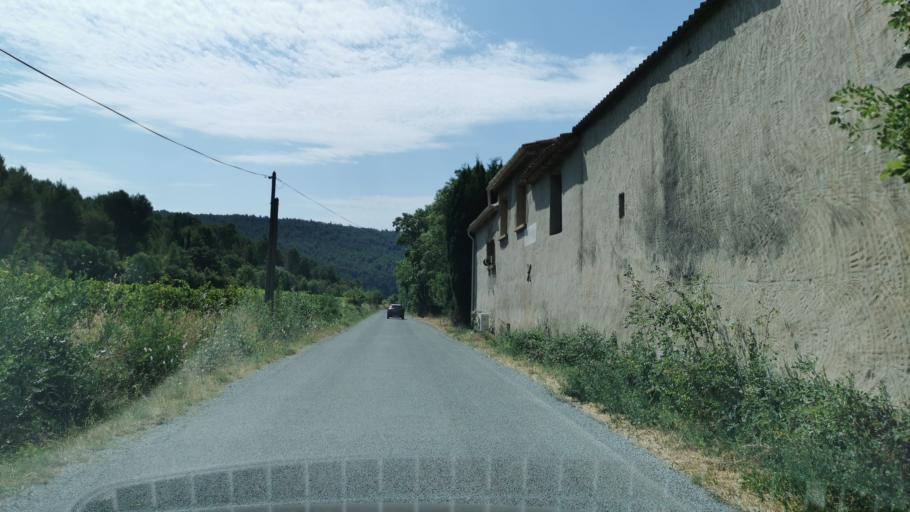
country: FR
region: Languedoc-Roussillon
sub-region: Departement de l'Aude
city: Bize-Minervois
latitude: 43.3313
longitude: 2.8773
